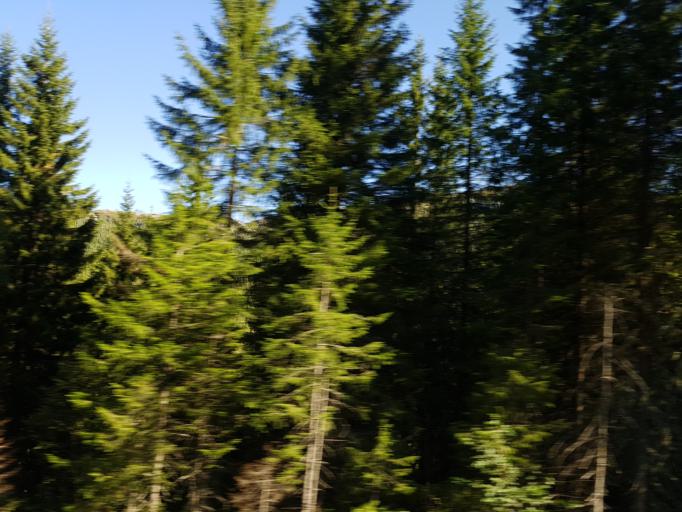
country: NO
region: Sor-Trondelag
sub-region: Afjord
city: A i Afjord
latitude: 63.7268
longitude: 10.2351
